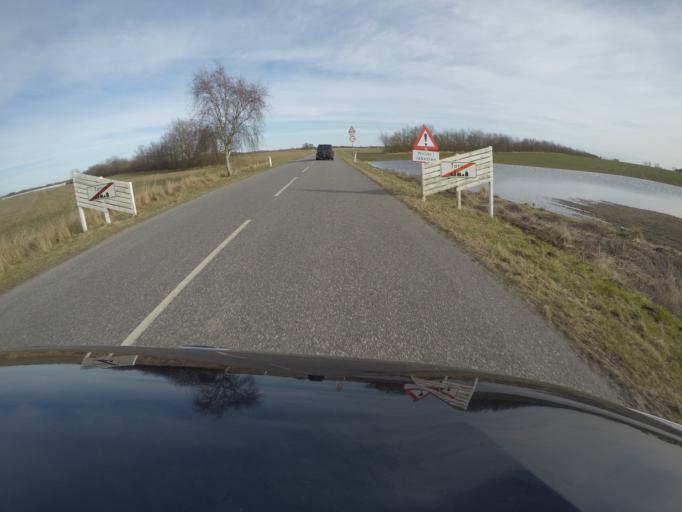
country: DK
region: Capital Region
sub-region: Halsnaes Kommune
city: Liseleje
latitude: 55.9835
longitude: 11.9468
